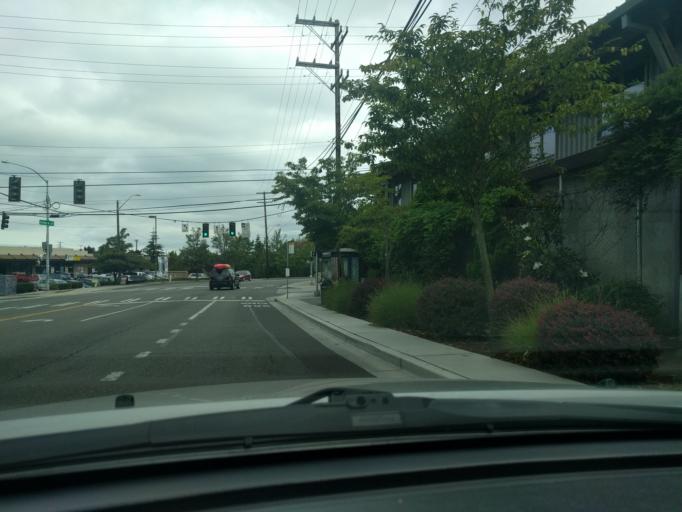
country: US
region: Washington
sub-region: King County
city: Seattle
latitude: 47.5680
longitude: -122.3632
